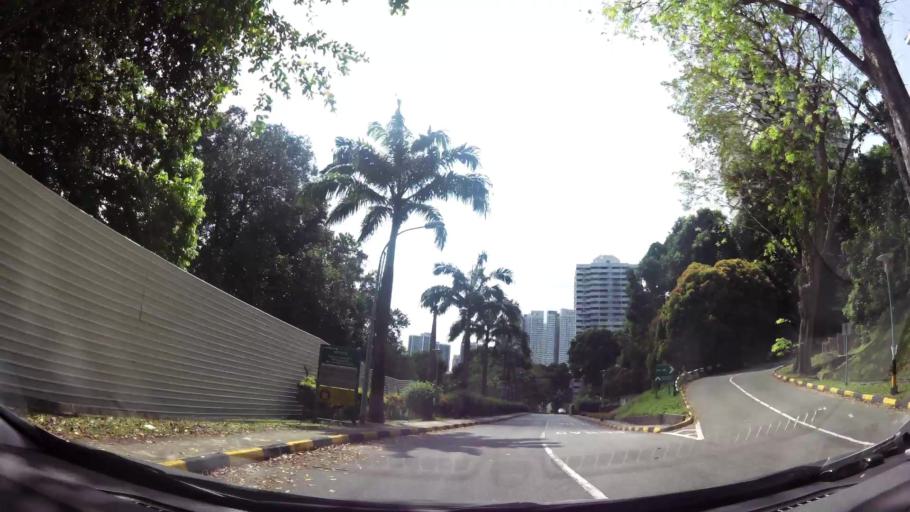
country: SG
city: Singapore
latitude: 1.3436
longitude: 103.8419
